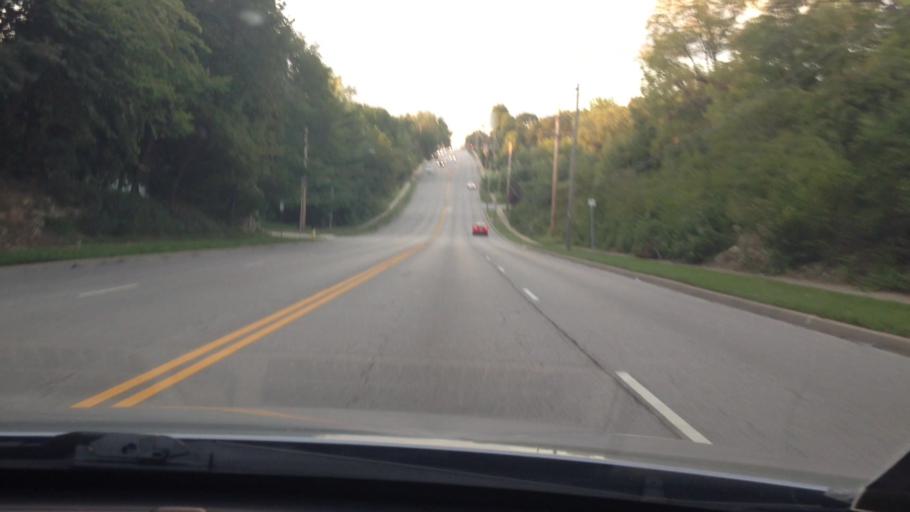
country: US
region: Missouri
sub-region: Jackson County
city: Raytown
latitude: 38.9692
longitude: -94.4652
